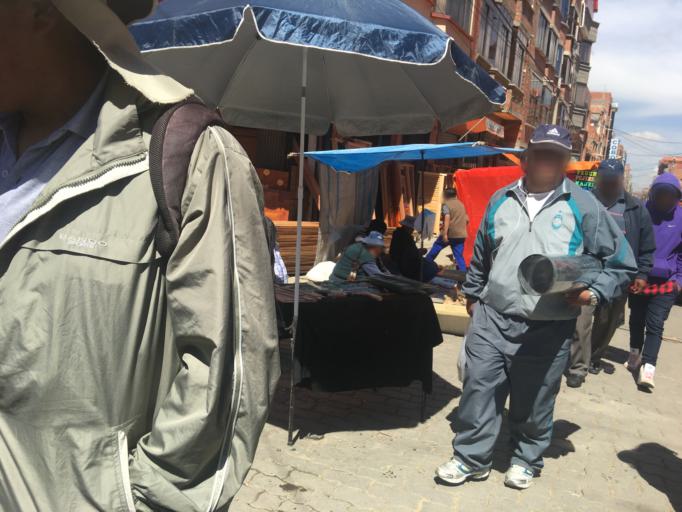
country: BO
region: La Paz
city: La Paz
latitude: -16.4948
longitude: -68.1693
